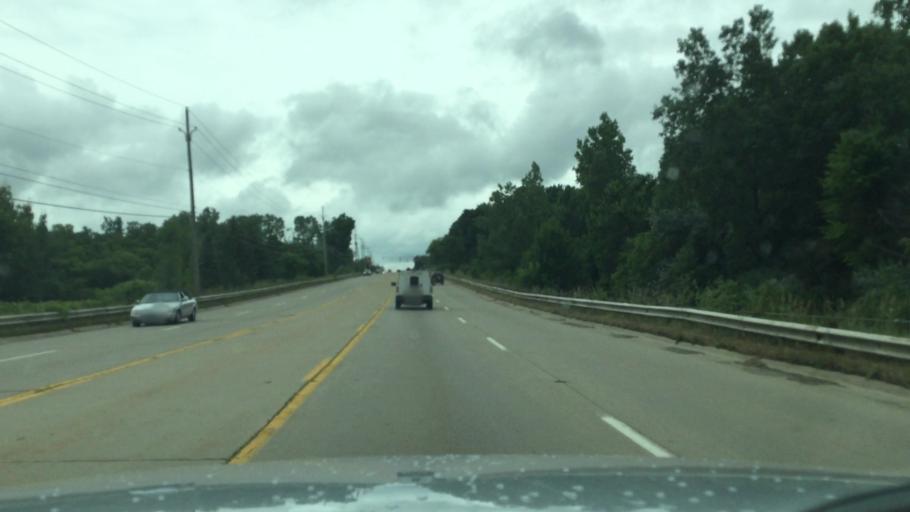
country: US
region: Michigan
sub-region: Genesee County
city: Flushing
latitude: 43.0353
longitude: -83.7736
